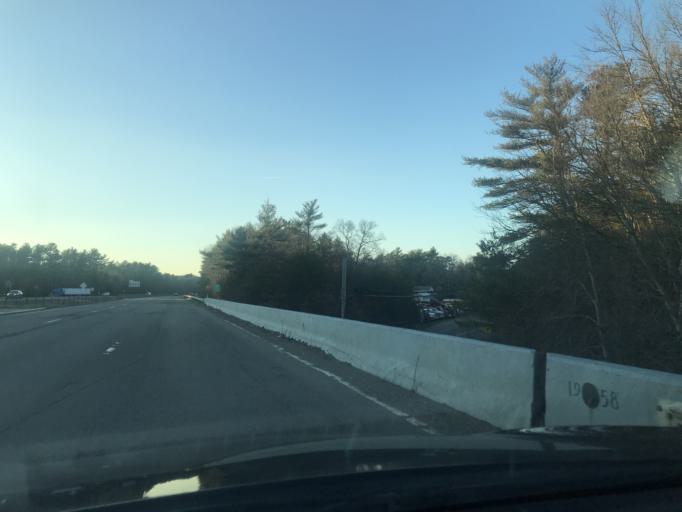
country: US
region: Massachusetts
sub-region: Plymouth County
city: Middleborough Center
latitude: 41.8465
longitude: -70.8495
